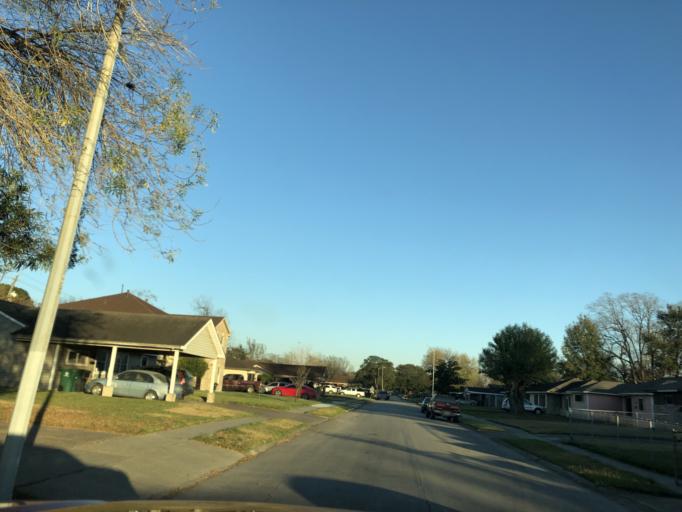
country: US
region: Texas
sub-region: Harris County
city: Jacinto City
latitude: 29.7626
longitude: -95.2722
